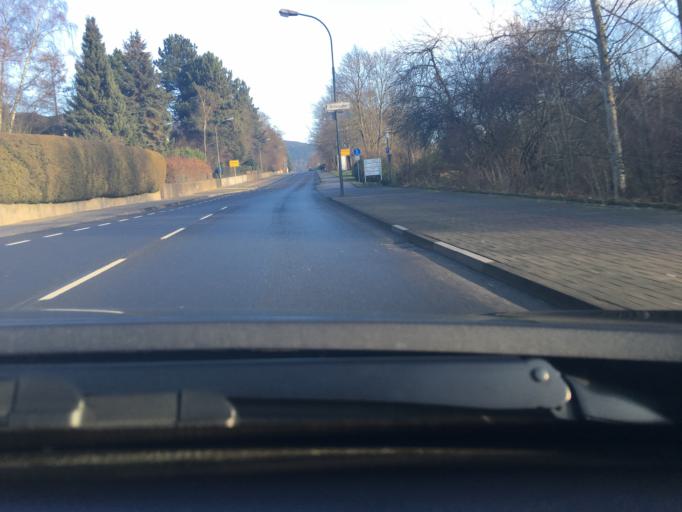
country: DE
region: Hesse
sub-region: Regierungsbezirk Kassel
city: Petersberg
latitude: 50.5584
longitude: 9.6992
